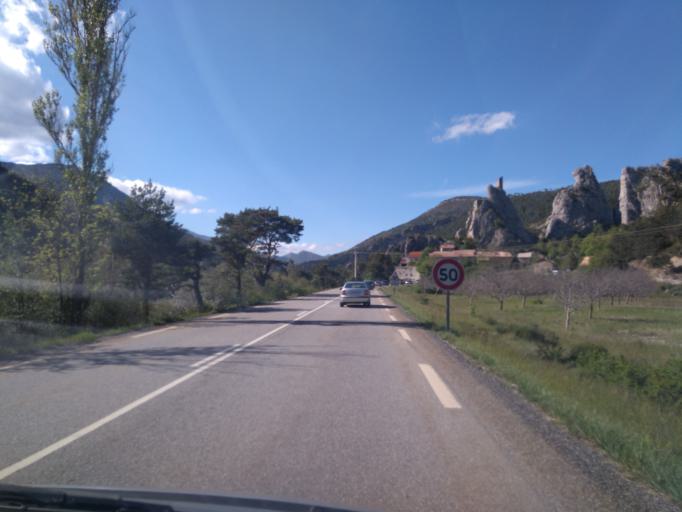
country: FR
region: Provence-Alpes-Cote d'Azur
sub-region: Departement des Hautes-Alpes
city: Veynes
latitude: 44.5855
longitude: 5.7219
